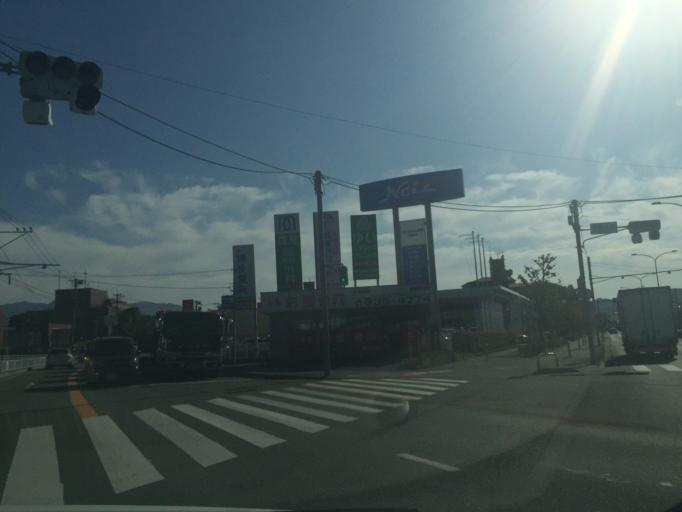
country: JP
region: Fukuoka
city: Umi
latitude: 33.5927
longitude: 130.4772
